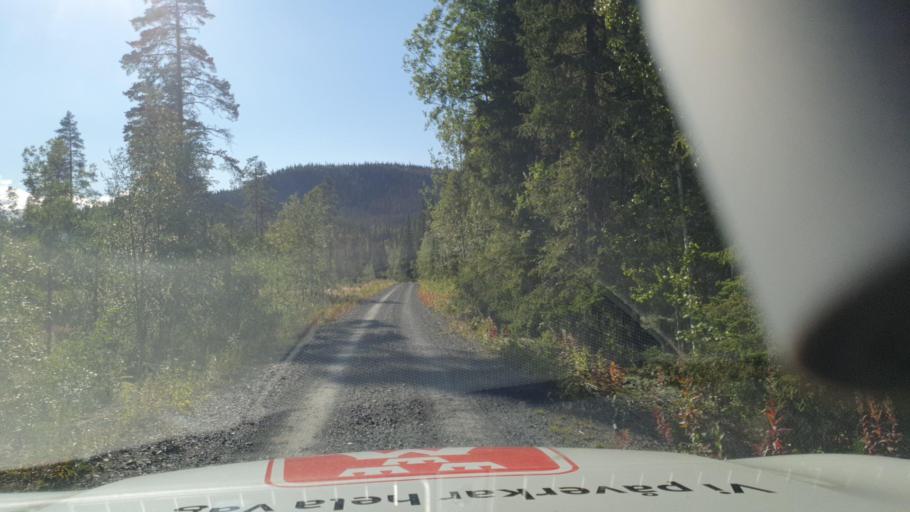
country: SE
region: Jaemtland
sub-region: Stroemsunds Kommun
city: Stroemsund
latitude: 64.5149
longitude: 15.3333
